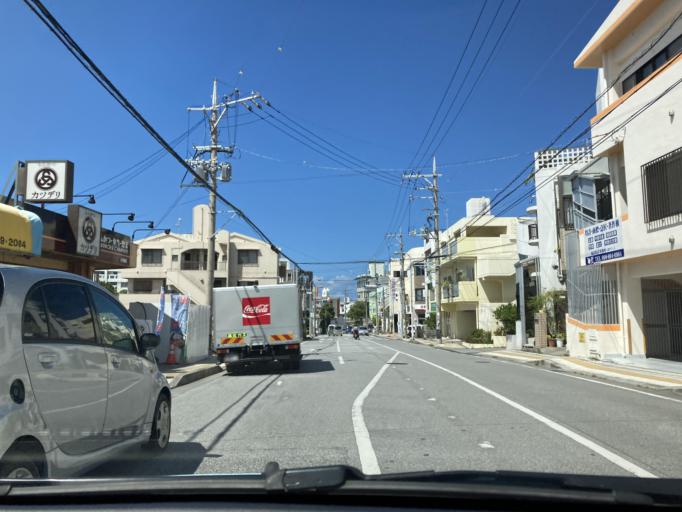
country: JP
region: Okinawa
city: Tomigusuku
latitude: 26.1933
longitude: 127.6666
